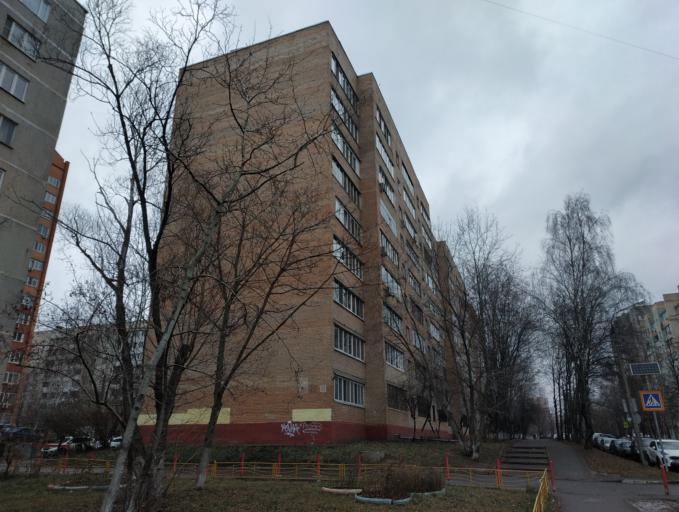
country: RU
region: Moskovskaya
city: Reutov
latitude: 55.7480
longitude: 37.8671
